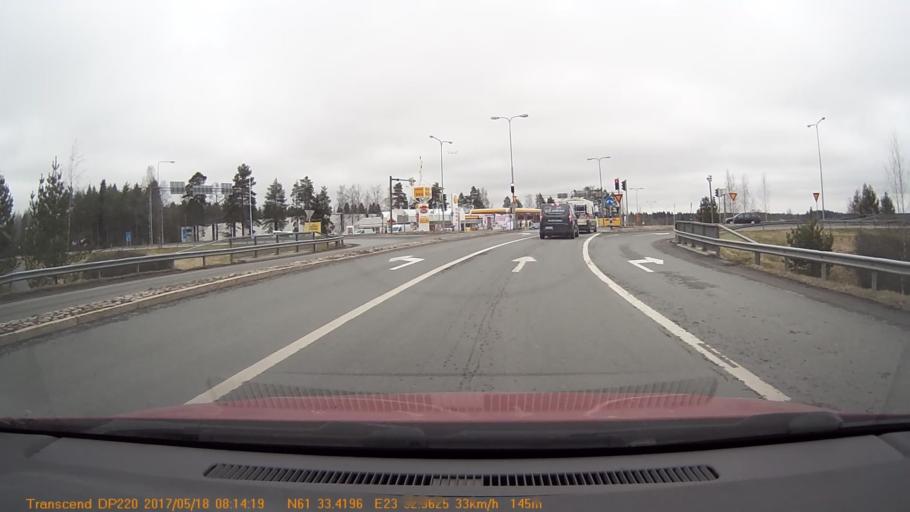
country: FI
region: Pirkanmaa
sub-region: Tampere
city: Yloejaervi
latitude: 61.5570
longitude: 23.5493
